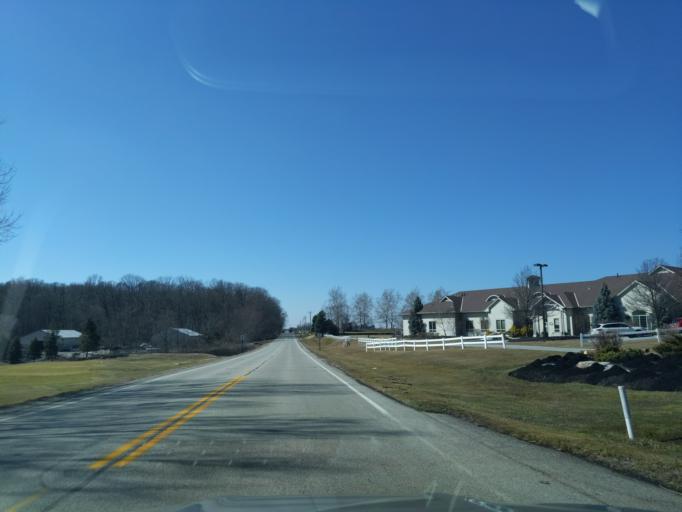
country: US
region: Indiana
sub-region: Tippecanoe County
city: West Lafayette
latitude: 40.4388
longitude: -86.9263
